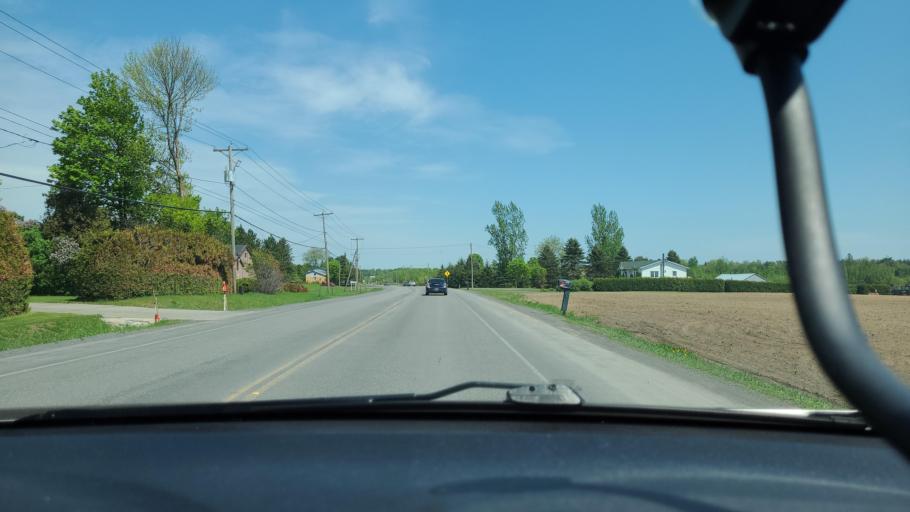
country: CA
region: Quebec
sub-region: Laurentides
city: Lachute
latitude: 45.6678
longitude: -74.2261
